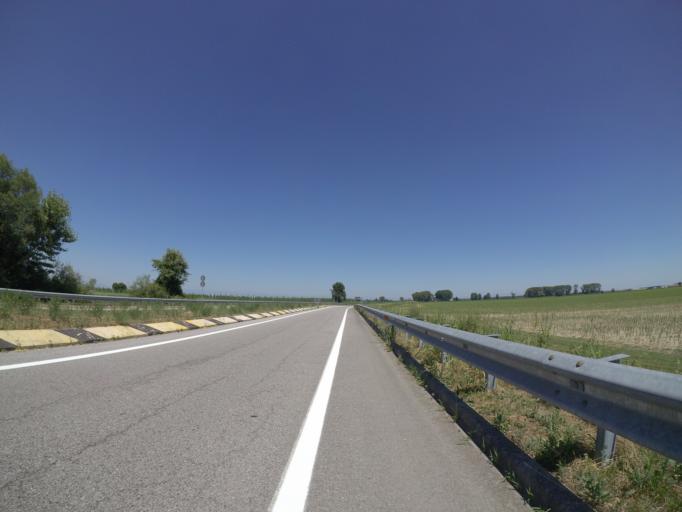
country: IT
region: Friuli Venezia Giulia
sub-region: Provincia di Udine
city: Ronchis
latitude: 45.8389
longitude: 13.0018
